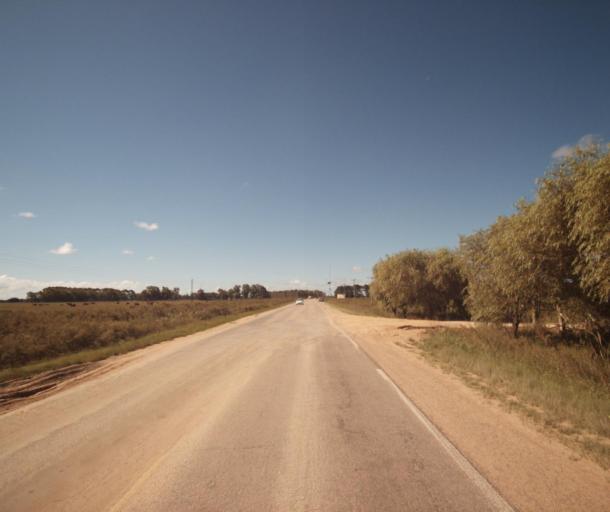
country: BR
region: Rio Grande do Sul
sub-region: Santa Vitoria Do Palmar
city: Santa Vitoria do Palmar
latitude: -33.5626
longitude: -53.3720
